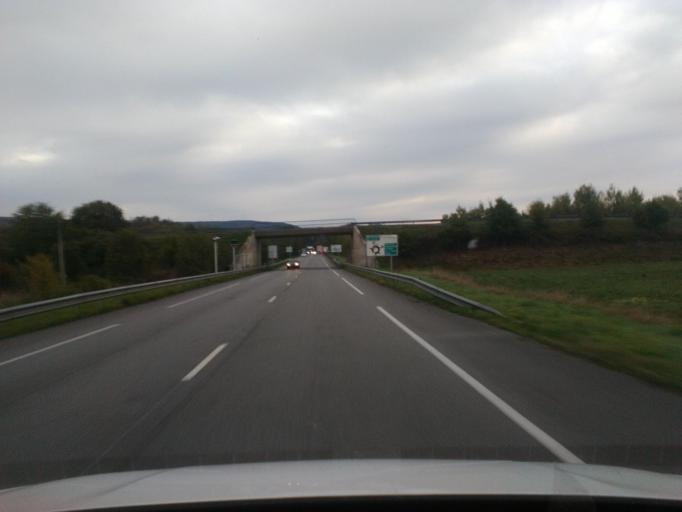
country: FR
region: Lorraine
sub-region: Departement des Vosges
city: Ban-de-Laveline
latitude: 48.2893
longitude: 7.0704
